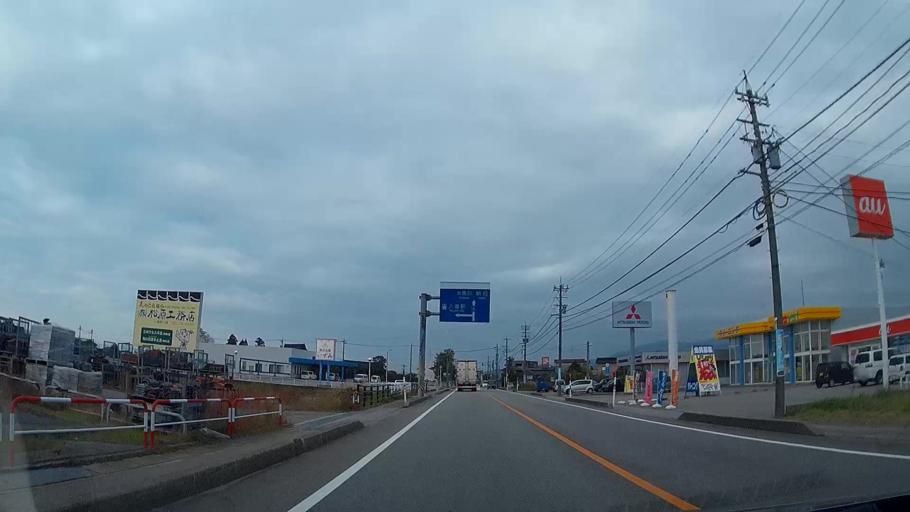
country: JP
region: Toyama
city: Nyuzen
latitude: 36.9373
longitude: 137.5093
